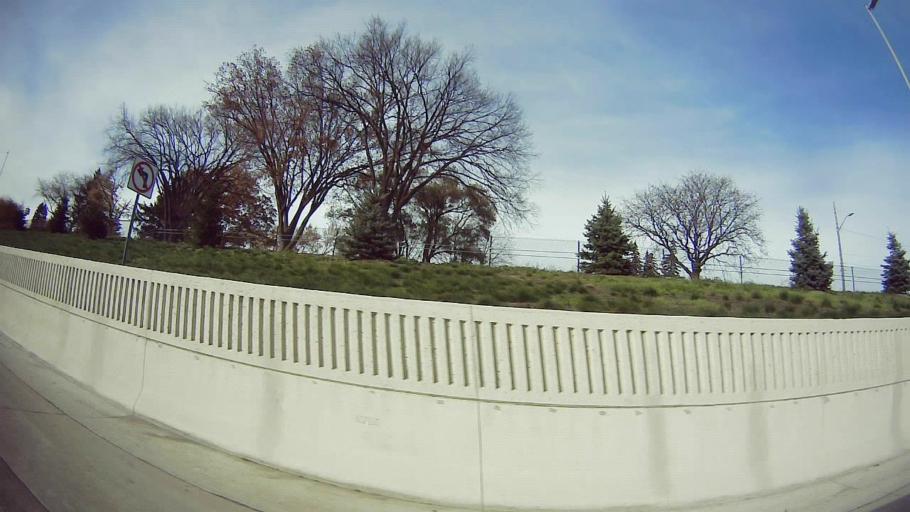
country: US
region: Michigan
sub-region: Wayne County
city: Redford
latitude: 42.3856
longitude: -83.2796
